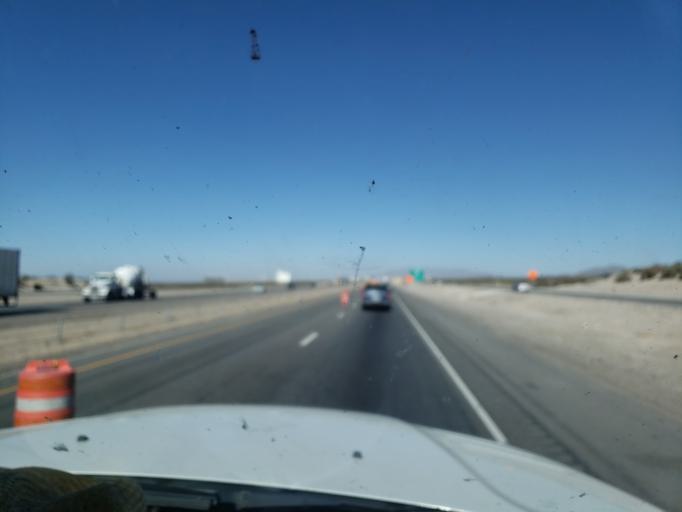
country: US
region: Texas
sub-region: El Paso County
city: Westway
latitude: 31.9338
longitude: -106.5827
